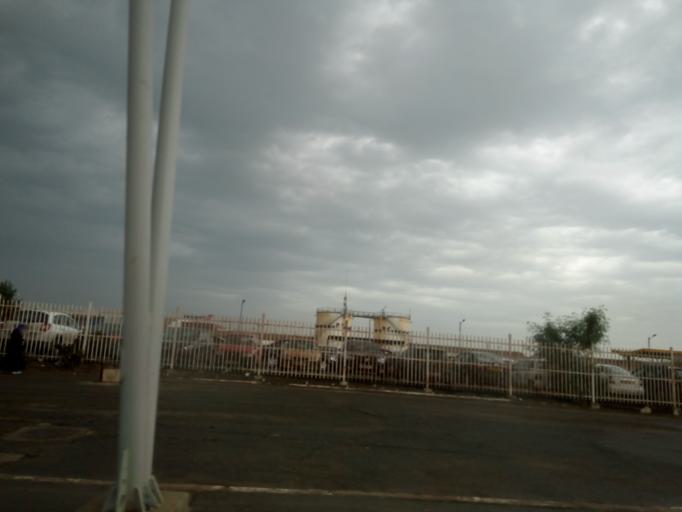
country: DZ
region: Alger
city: Dar el Beida
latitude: 36.7021
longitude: 3.2106
